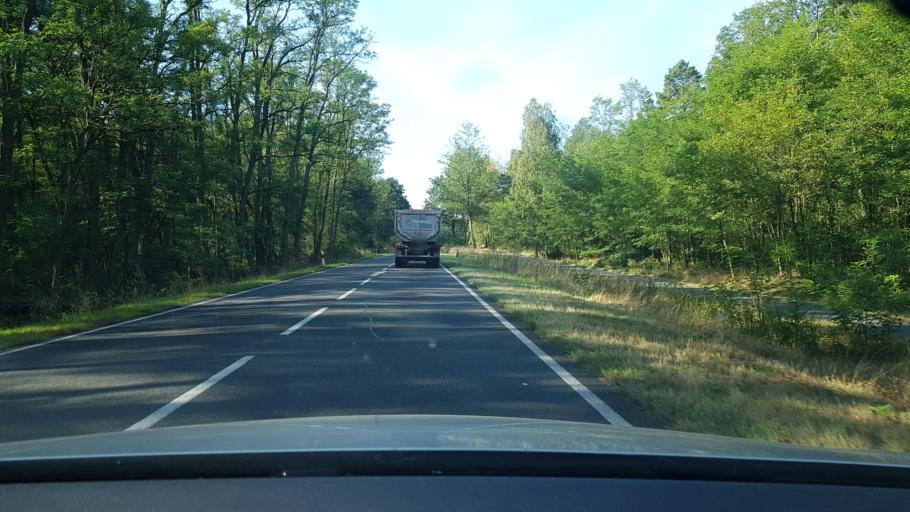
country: DE
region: Brandenburg
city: Eisenhuettenstadt
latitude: 52.1514
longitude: 14.5807
